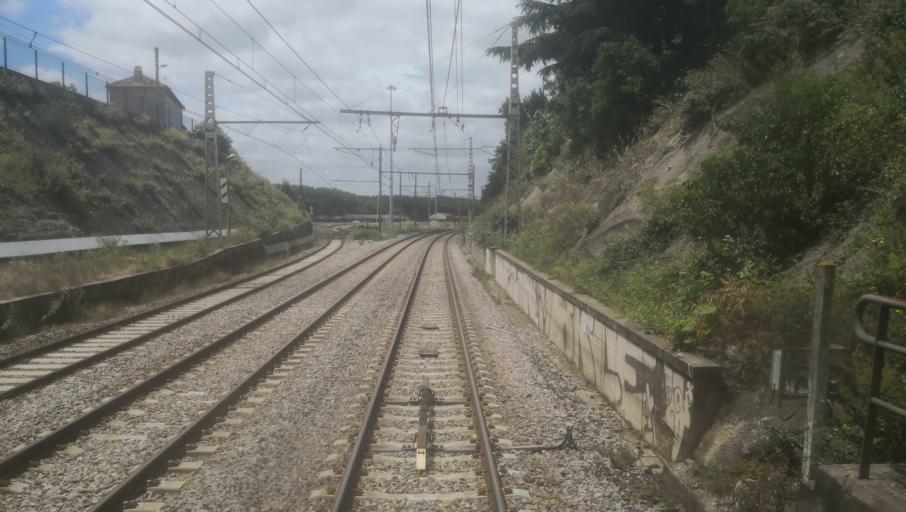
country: FR
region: Languedoc-Roussillon
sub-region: Departement de l'Aude
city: Carcassonne
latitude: 43.2177
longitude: 2.3417
